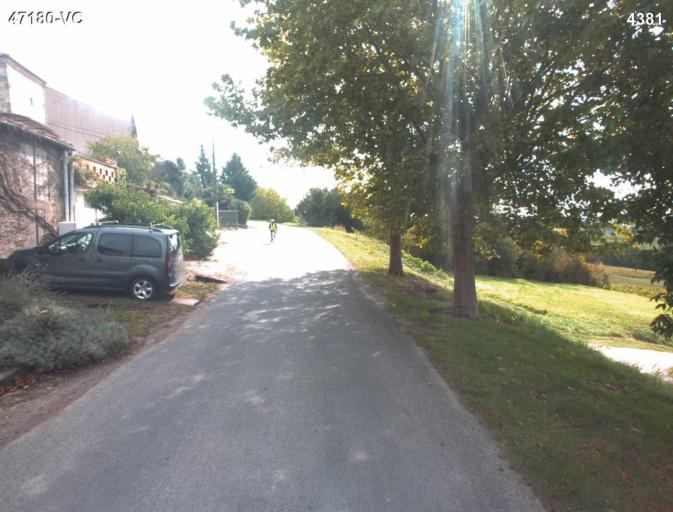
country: FR
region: Aquitaine
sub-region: Departement du Lot-et-Garonne
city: Sainte-Colombe-en-Bruilhois
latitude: 44.1603
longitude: 0.4595
